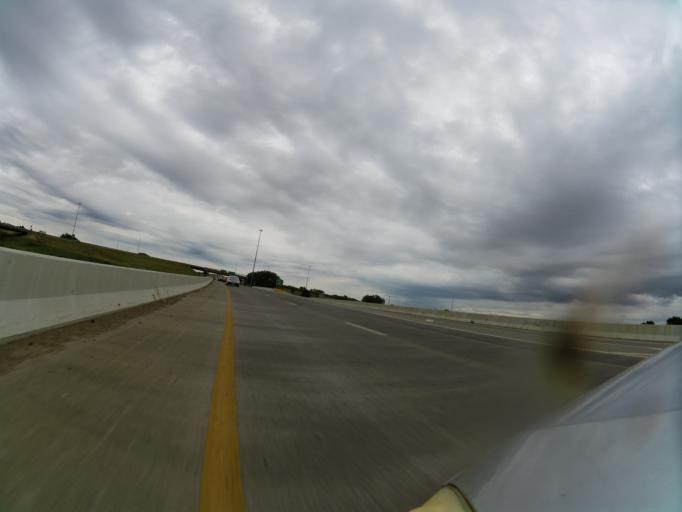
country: US
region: Kansas
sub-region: Sedgwick County
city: Wichita
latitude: 37.7539
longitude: -97.3795
